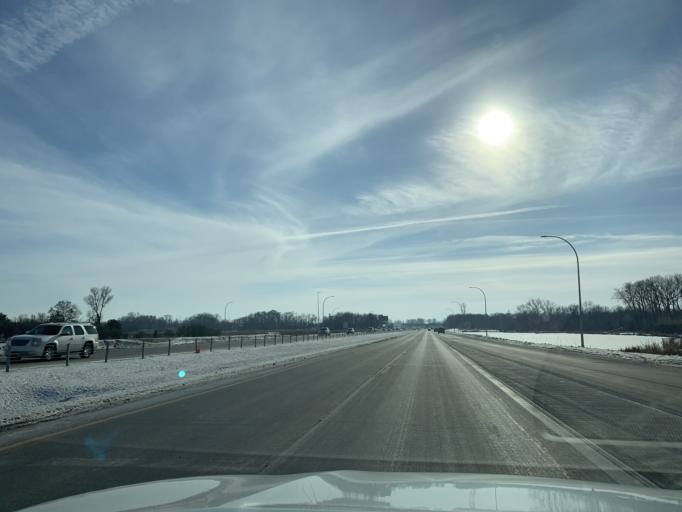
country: US
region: Minnesota
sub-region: Washington County
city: Forest Lake
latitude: 45.2896
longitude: -93.0031
